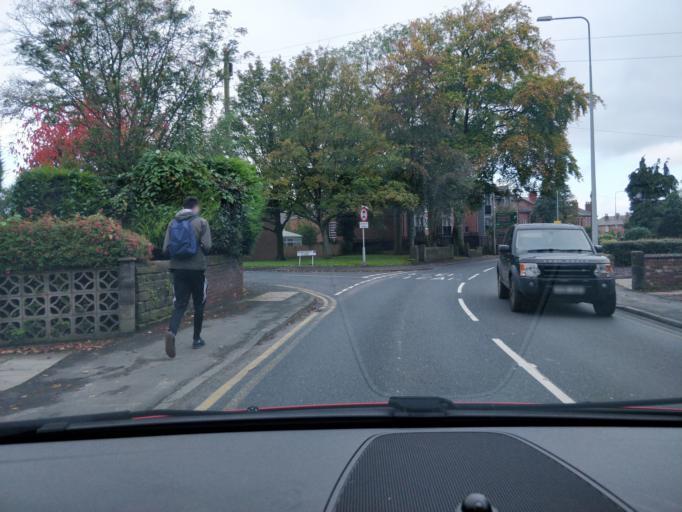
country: GB
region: England
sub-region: Lancashire
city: Ormskirk
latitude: 53.5705
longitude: -2.8898
